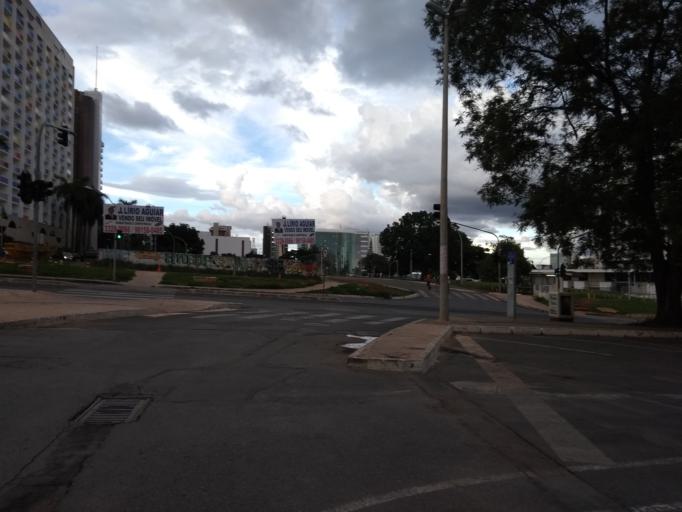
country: BR
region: Federal District
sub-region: Brasilia
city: Brasilia
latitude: -15.7963
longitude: -47.8885
